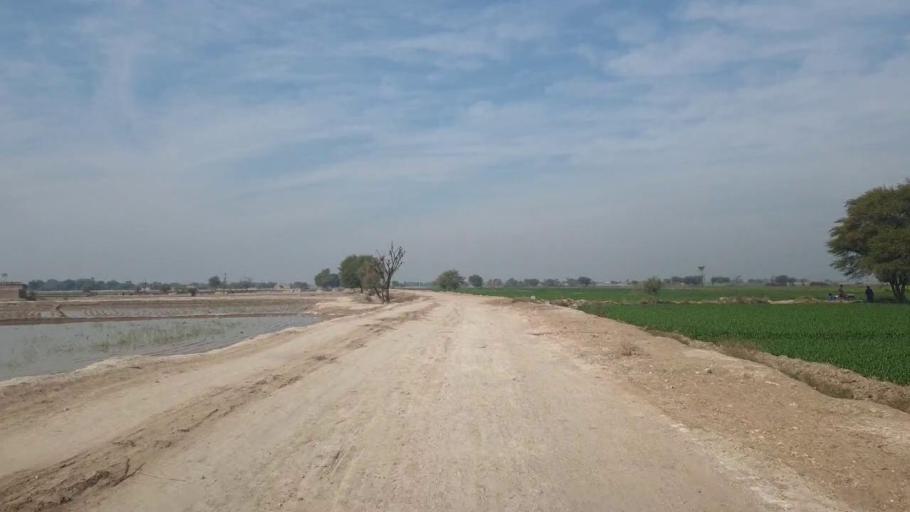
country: PK
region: Sindh
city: Nawabshah
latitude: 26.1623
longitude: 68.5071
